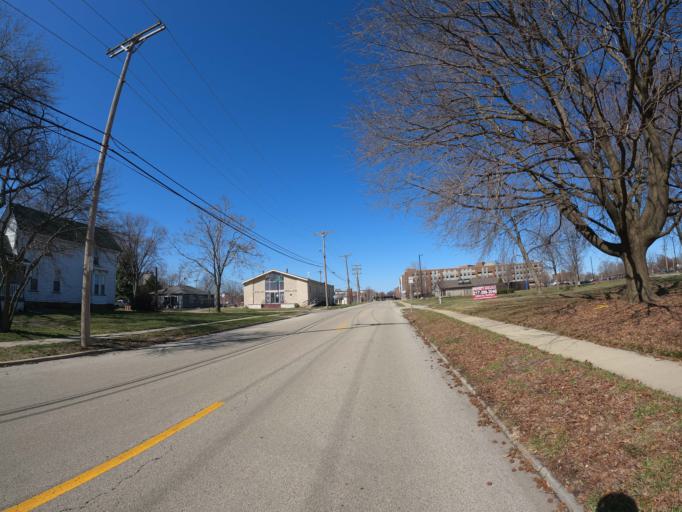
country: US
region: Illinois
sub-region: Sangamon County
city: Springfield
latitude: 39.8060
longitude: -89.6575
